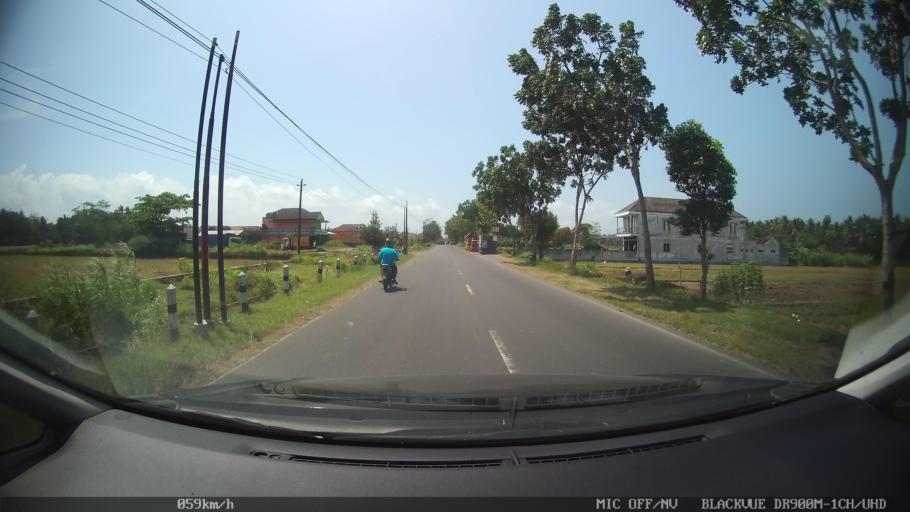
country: ID
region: Daerah Istimewa Yogyakarta
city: Srandakan
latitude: -7.9521
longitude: 110.2023
